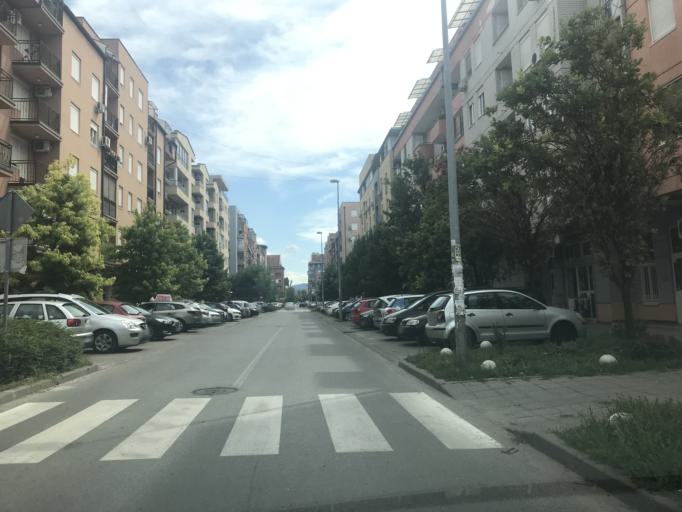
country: RS
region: Autonomna Pokrajina Vojvodina
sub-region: Juznobacki Okrug
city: Novi Sad
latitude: 45.2586
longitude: 19.8125
